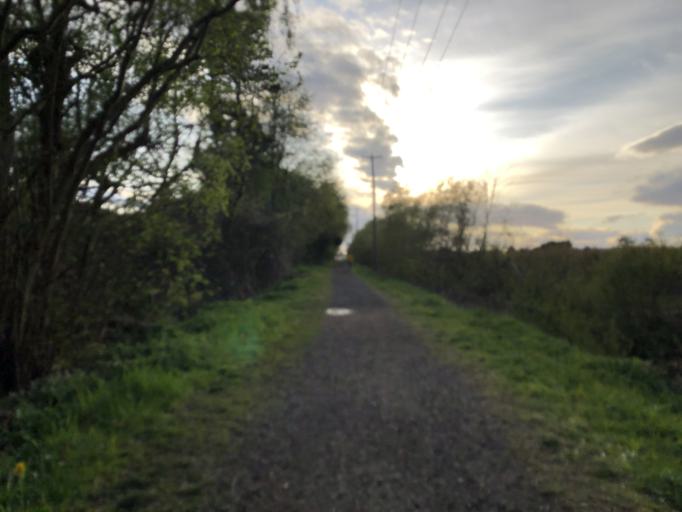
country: CA
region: British Columbia
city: Richmond
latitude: 49.1480
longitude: -123.1083
